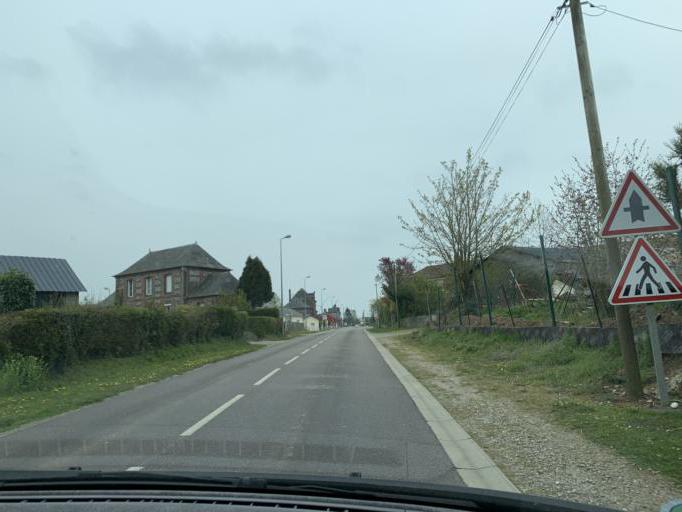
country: FR
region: Haute-Normandie
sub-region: Departement de la Seine-Maritime
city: Londinieres
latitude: 49.8426
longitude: 1.4743
